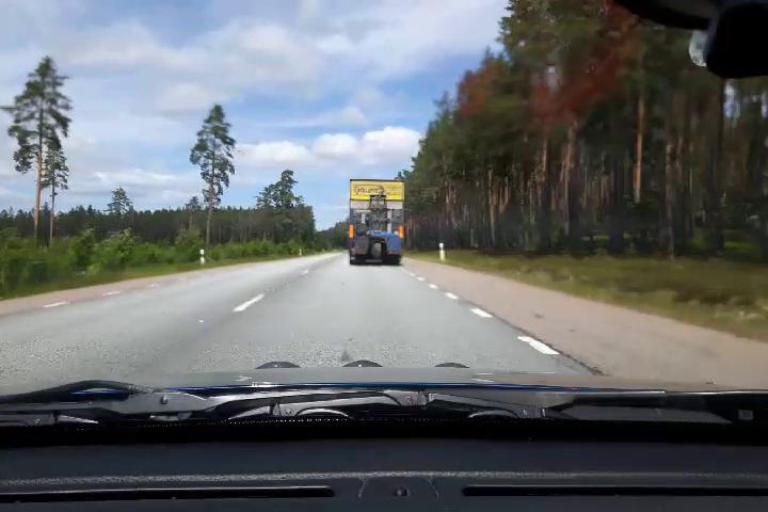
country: SE
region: Uppsala
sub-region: Tierps Kommun
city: Tierp
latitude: 60.1958
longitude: 17.4801
